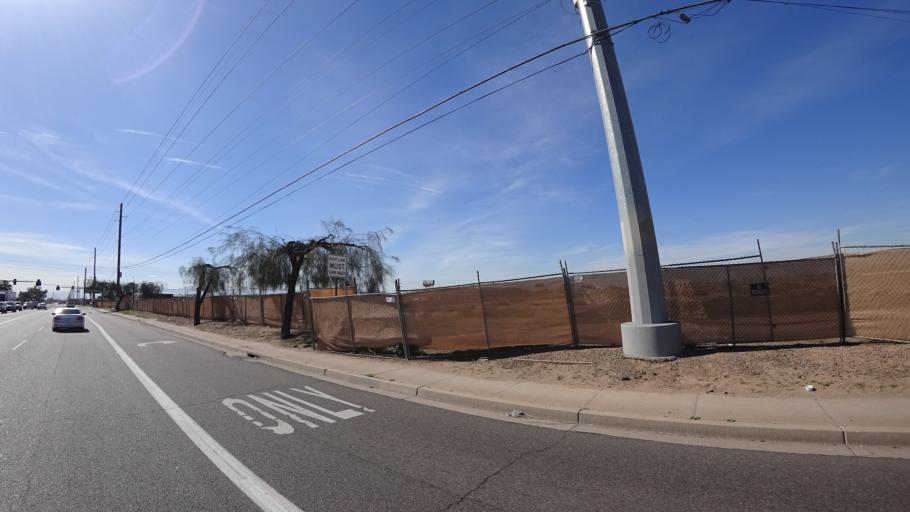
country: US
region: Arizona
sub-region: Maricopa County
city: Tolleson
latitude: 33.4528
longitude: -112.1867
